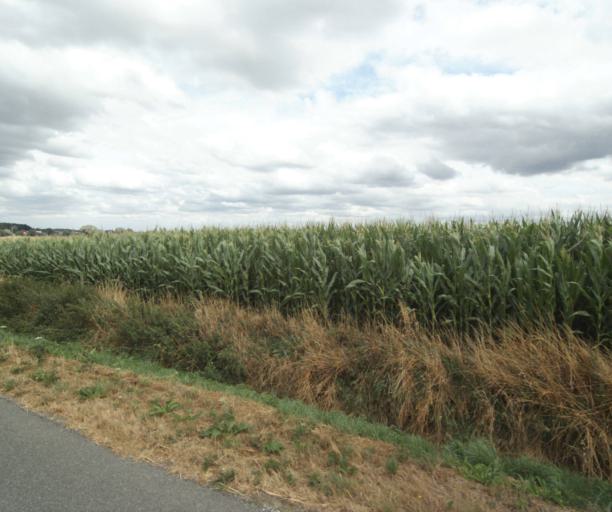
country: FR
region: Nord-Pas-de-Calais
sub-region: Departement du Nord
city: Linselles
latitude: 50.7522
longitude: 3.0781
